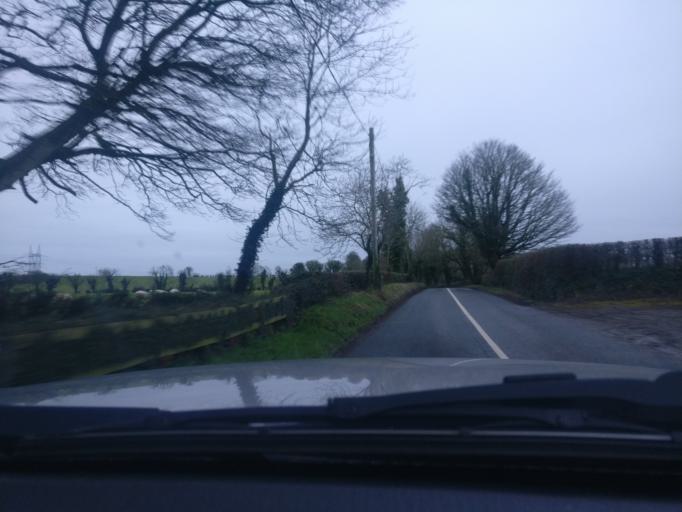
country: IE
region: Leinster
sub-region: An Mhi
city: Dunshaughlin
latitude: 53.4796
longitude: -6.6165
